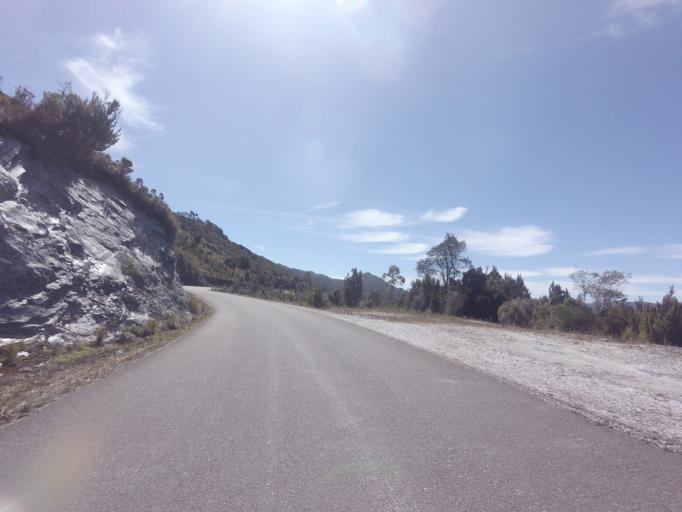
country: AU
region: Tasmania
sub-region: West Coast
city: Queenstown
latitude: -42.7383
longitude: 145.9819
